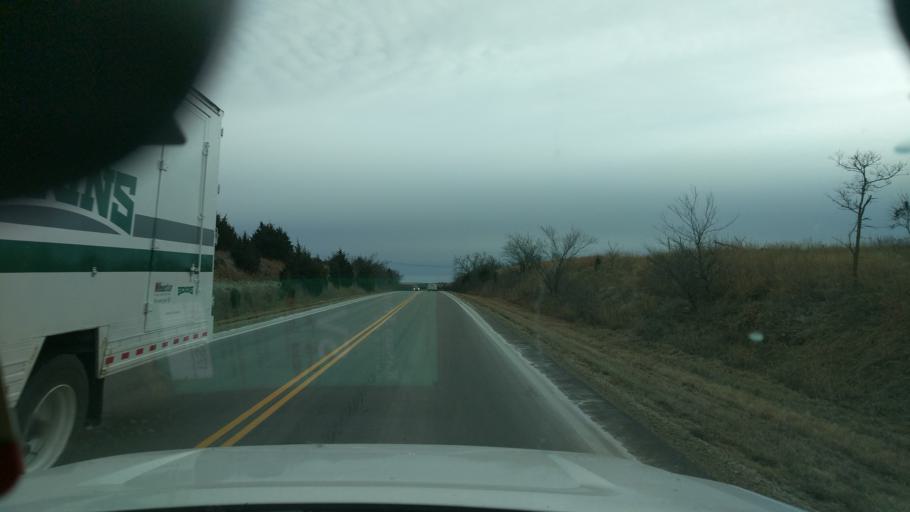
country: US
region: Kansas
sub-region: Geary County
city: Junction City
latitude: 38.9648
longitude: -96.8572
